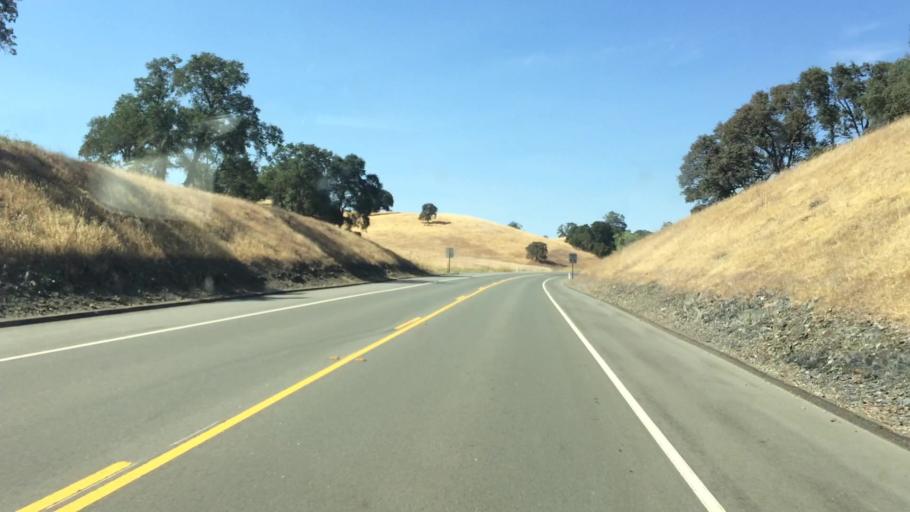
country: US
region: California
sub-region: Amador County
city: Plymouth
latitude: 38.4354
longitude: -120.8773
